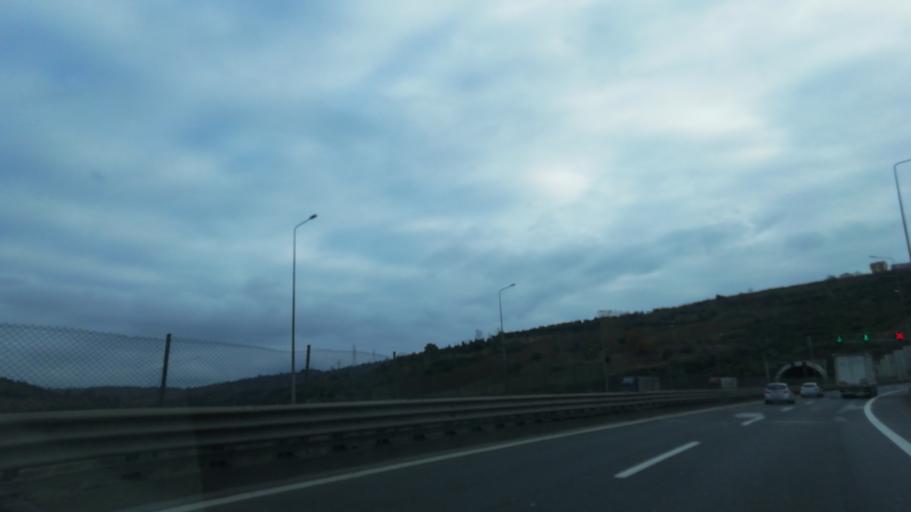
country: TR
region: Kocaeli
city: Izmit
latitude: 40.7791
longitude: 29.8856
